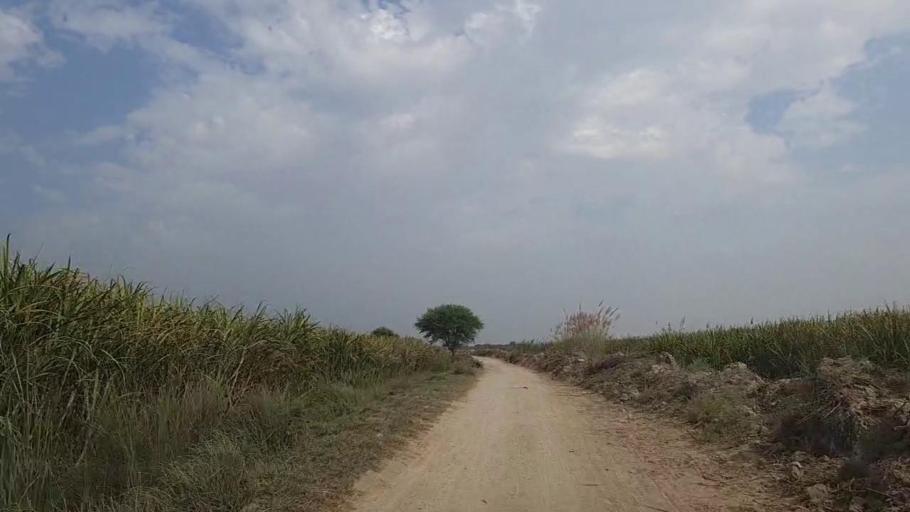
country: PK
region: Sindh
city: Daro Mehar
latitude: 24.7077
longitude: 68.1455
